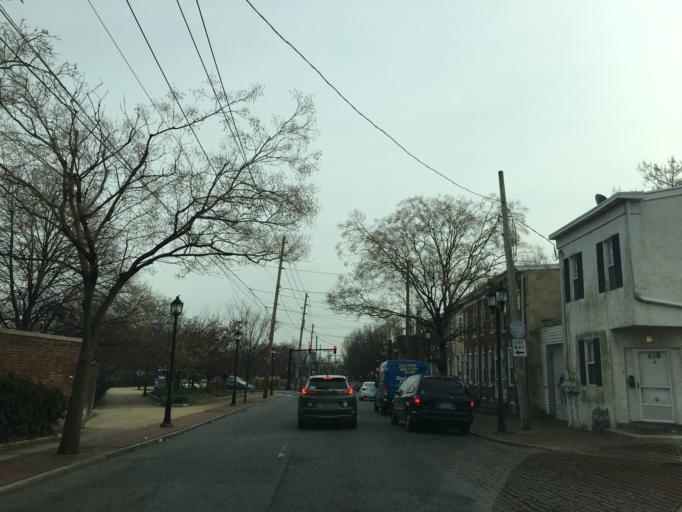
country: US
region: Delaware
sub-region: New Castle County
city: Wilmington
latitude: 39.7437
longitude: -75.5405
